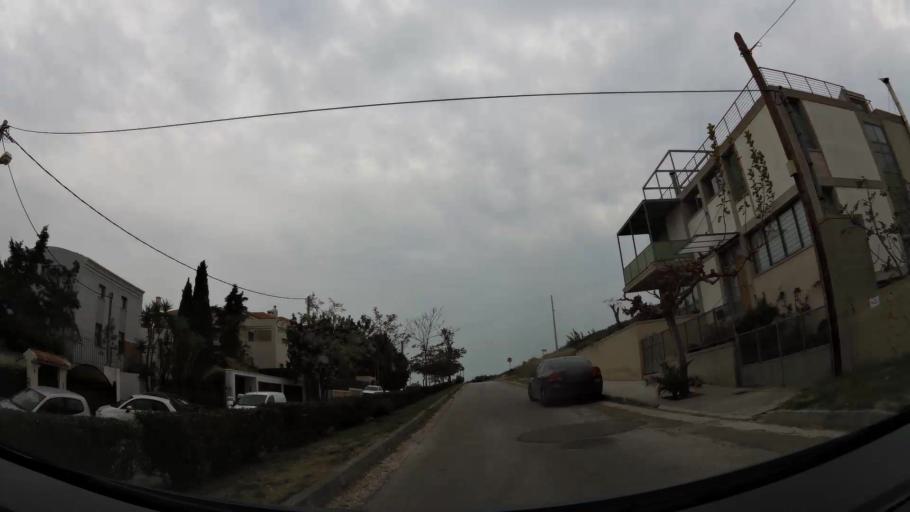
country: GR
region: Attica
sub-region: Nomarchia Athinas
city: Alimos
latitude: 37.9119
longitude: 23.7300
